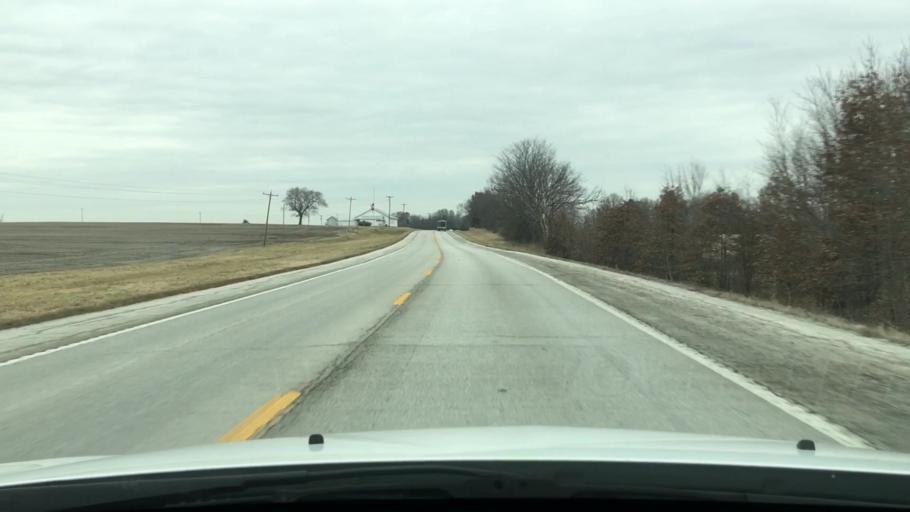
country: US
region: Missouri
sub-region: Montgomery County
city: Wellsville
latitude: 39.2027
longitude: -91.6463
